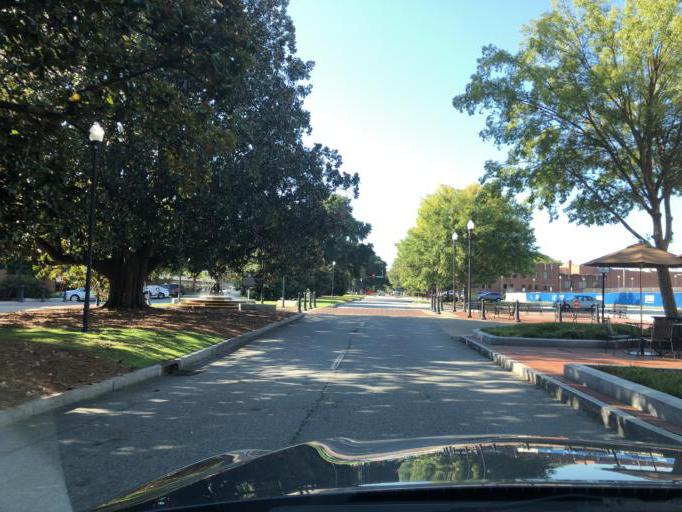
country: US
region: Alabama
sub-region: Russell County
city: Phenix City
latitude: 32.4719
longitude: -84.9933
